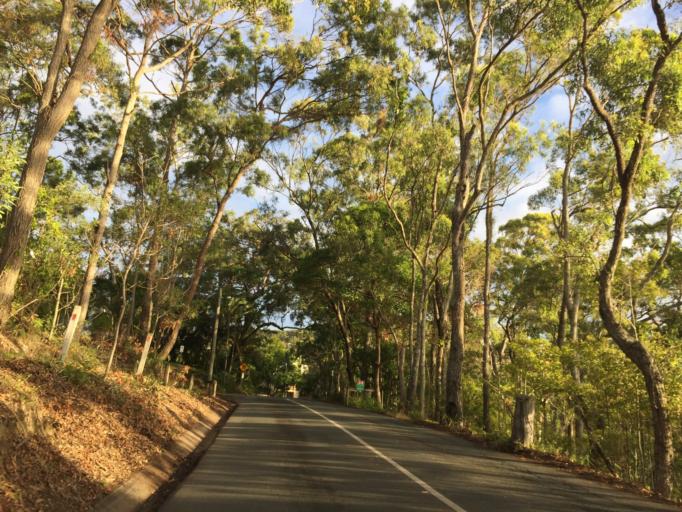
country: AU
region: Queensland
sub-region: Sunshine Coast
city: Noosa Heads
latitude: -26.3826
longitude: 153.0974
